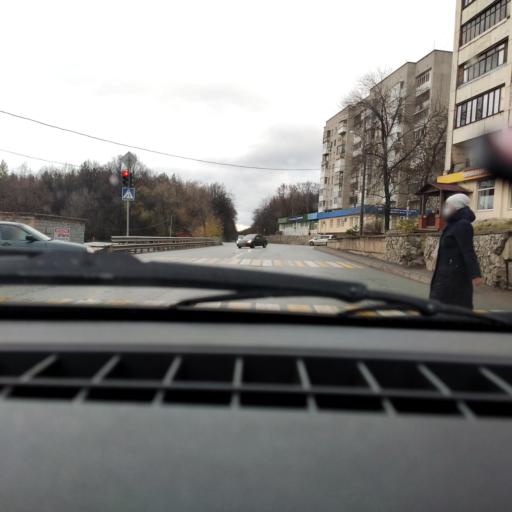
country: RU
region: Bashkortostan
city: Ufa
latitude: 54.7801
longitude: 56.0234
